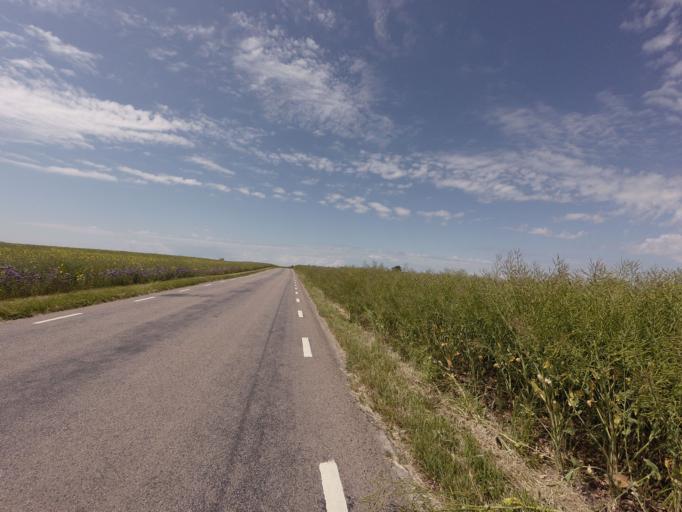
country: SE
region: Skane
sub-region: Trelleborgs Kommun
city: Skare
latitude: 55.4242
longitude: 13.0989
